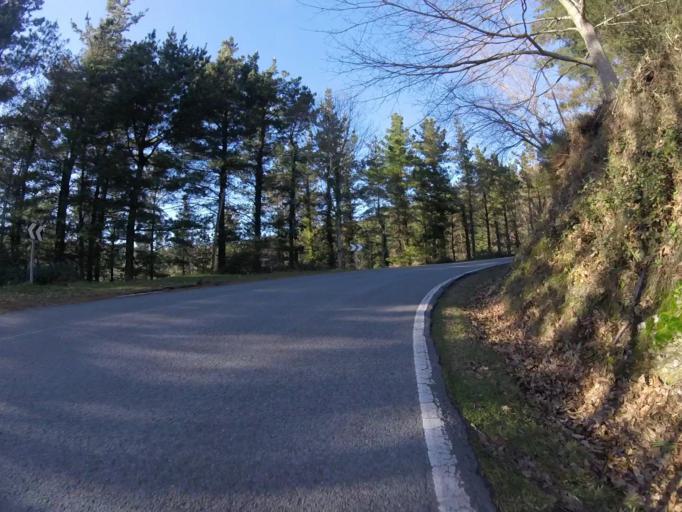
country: ES
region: Navarre
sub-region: Provincia de Navarra
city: Lesaka
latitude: 43.2655
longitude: -1.7411
